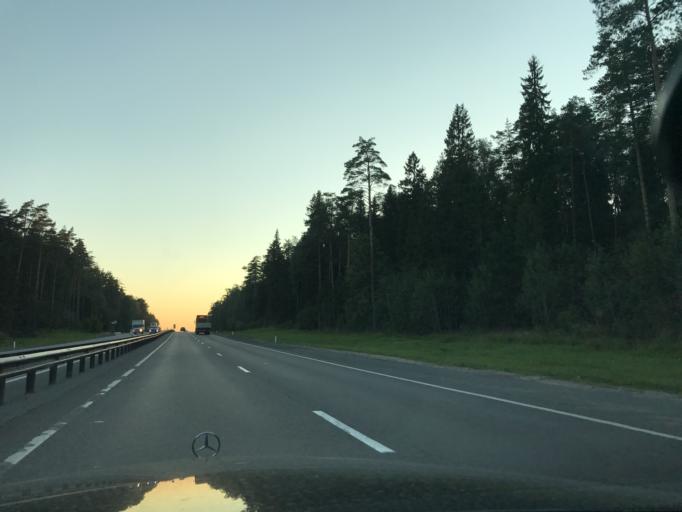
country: RU
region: Vladimir
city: Petushki
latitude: 55.9309
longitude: 39.3619
